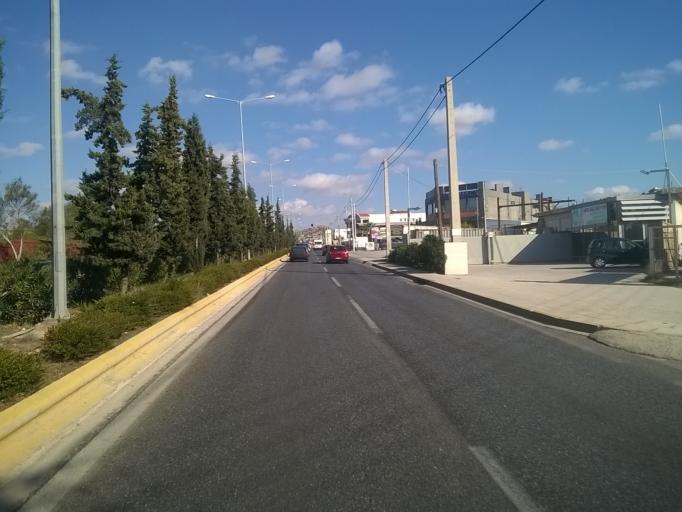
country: GR
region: Attica
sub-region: Nomarchia Anatolikis Attikis
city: Vari
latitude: 37.8397
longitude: 23.8131
